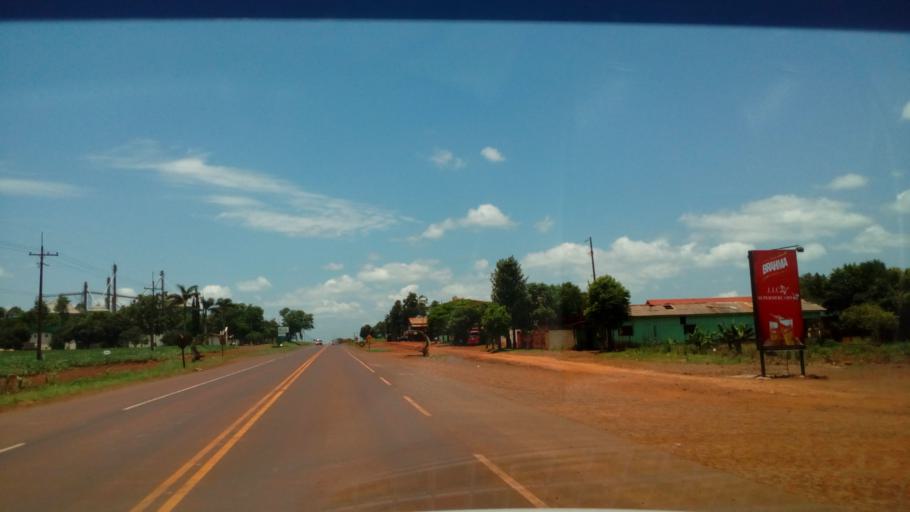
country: PY
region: Alto Parana
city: Naranjal
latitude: -25.9328
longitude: -55.1164
